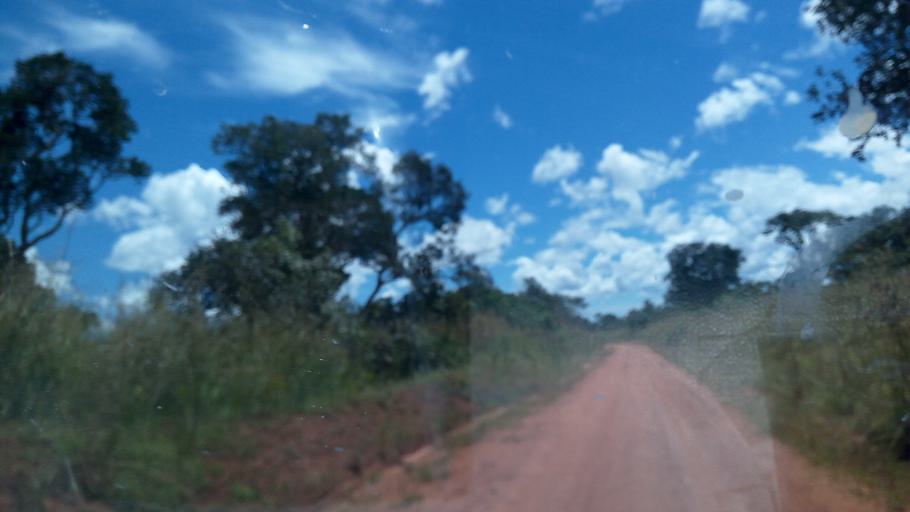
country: CD
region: Katanga
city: Kalemie
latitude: -5.4253
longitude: 28.9368
